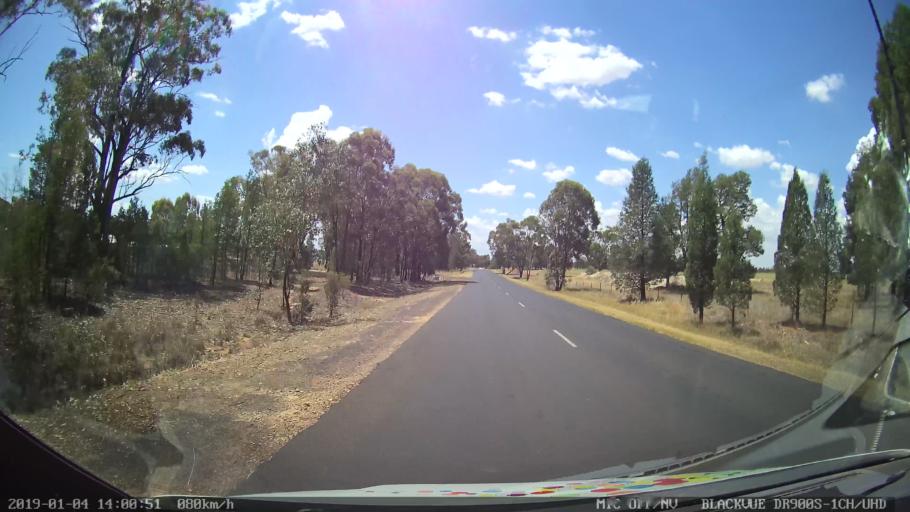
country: AU
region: New South Wales
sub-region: Dubbo Municipality
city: Dubbo
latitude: -32.3028
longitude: 148.5960
